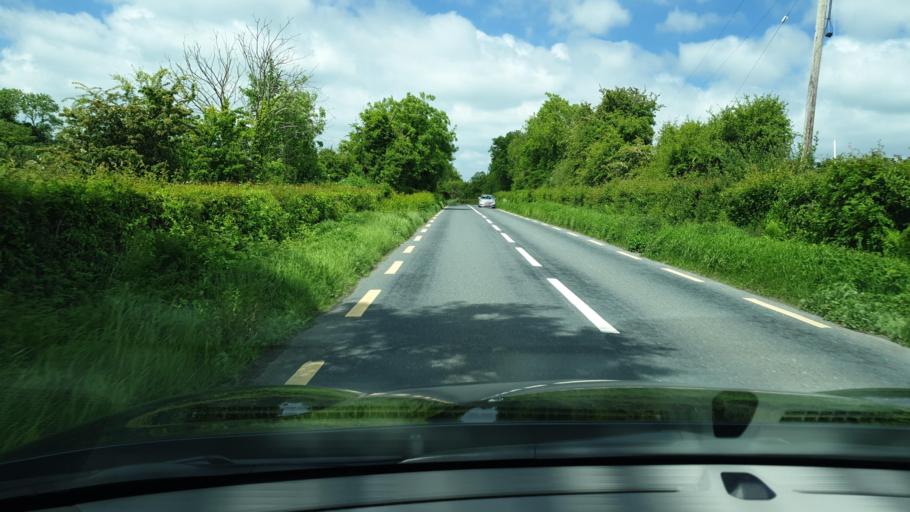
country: IE
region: Ulster
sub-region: An Cabhan
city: Kingscourt
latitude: 53.8930
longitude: -6.7579
